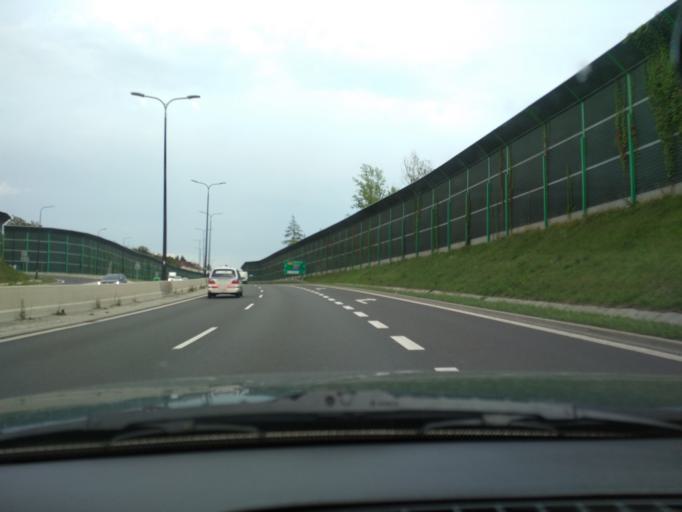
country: PL
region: Silesian Voivodeship
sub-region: Gliwice
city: Gliwice
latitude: 50.2914
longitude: 18.6916
